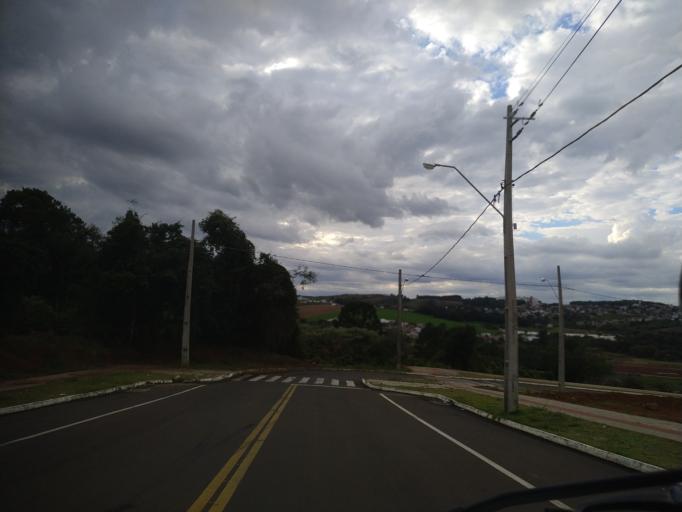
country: BR
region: Santa Catarina
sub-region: Chapeco
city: Chapeco
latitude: -27.0629
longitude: -52.6229
